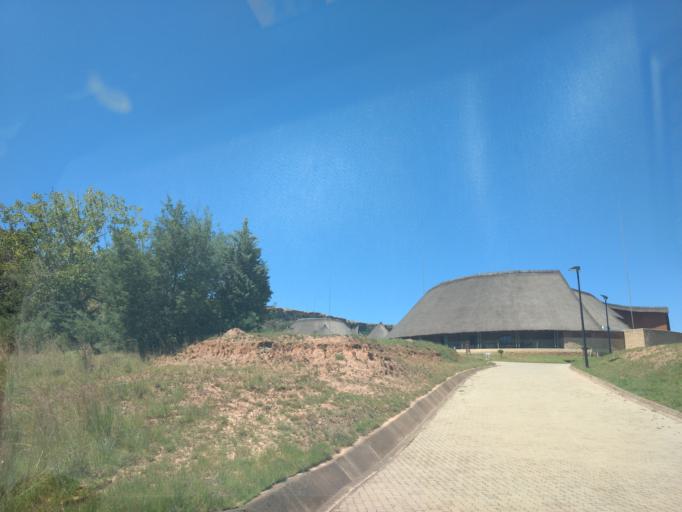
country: LS
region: Maseru
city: Maseru
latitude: -29.3442
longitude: 27.6622
